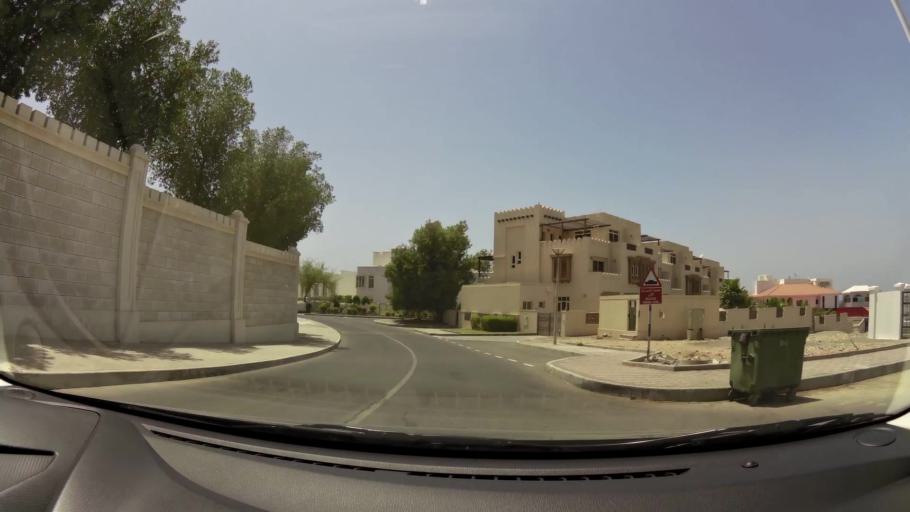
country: OM
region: Muhafazat Masqat
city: Muscat
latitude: 23.6306
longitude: 58.4876
